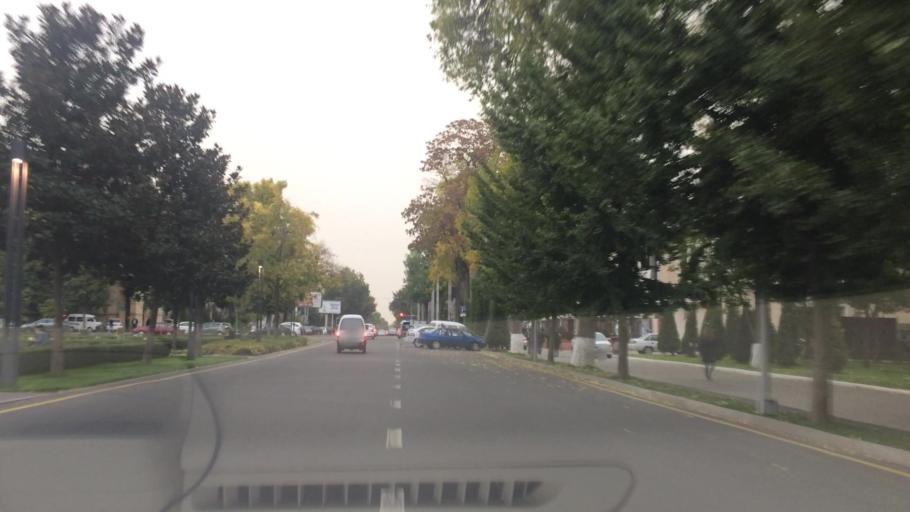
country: UZ
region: Toshkent Shahri
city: Tashkent
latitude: 41.3087
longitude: 69.2822
